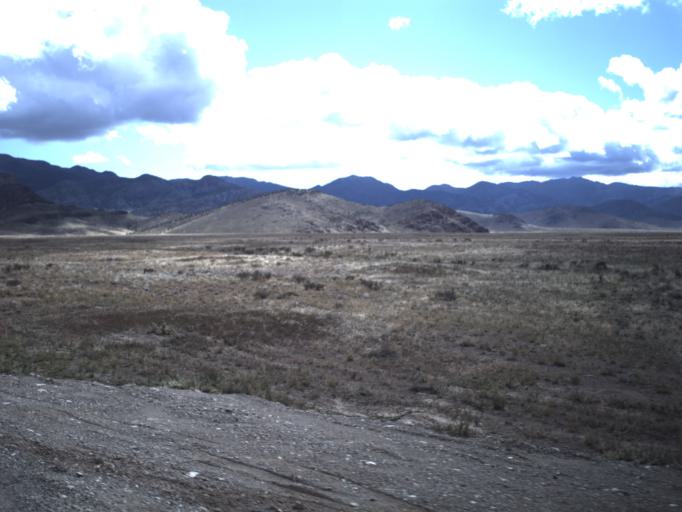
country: US
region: Utah
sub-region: Beaver County
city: Milford
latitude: 38.5095
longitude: -113.6203
